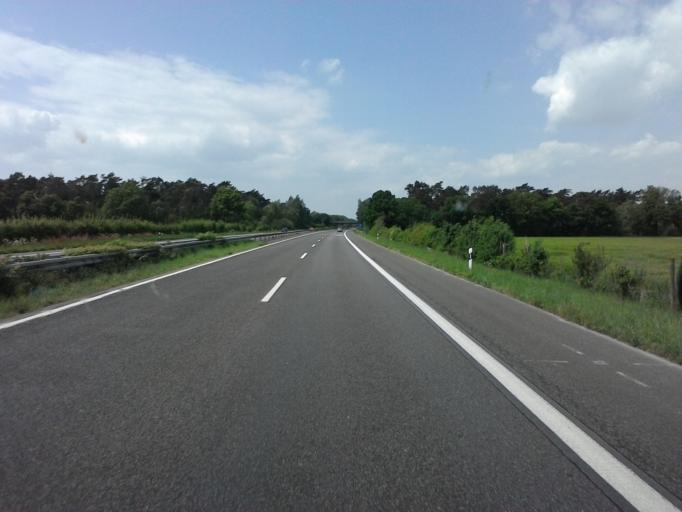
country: DE
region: North Rhine-Westphalia
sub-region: Regierungsbezirk Dusseldorf
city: Alpen
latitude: 51.5661
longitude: 6.4718
